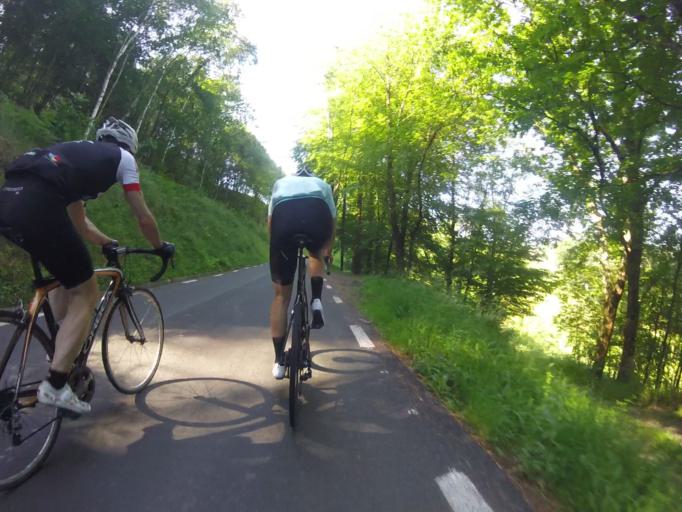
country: ES
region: Basque Country
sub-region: Provincia de Guipuzcoa
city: Beizama
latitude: 43.1359
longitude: -2.2247
